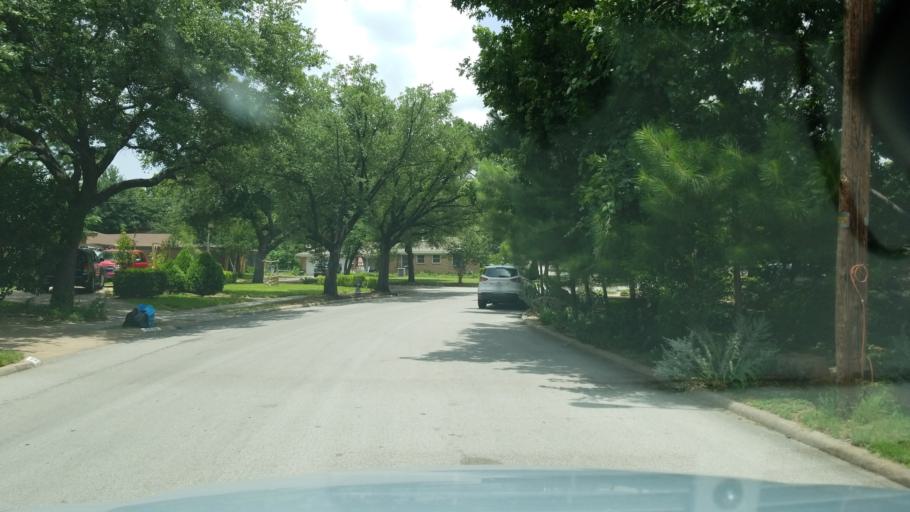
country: US
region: Texas
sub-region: Dallas County
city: Irving
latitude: 32.8244
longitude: -96.9239
